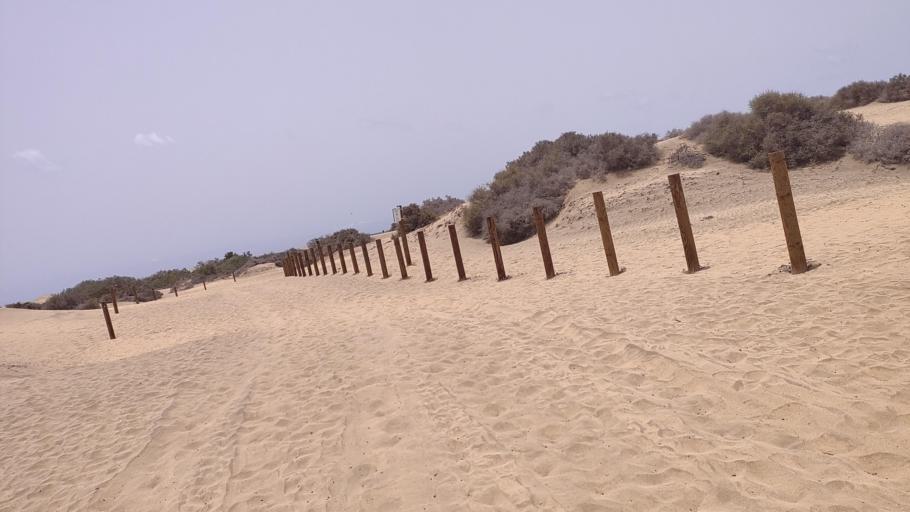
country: ES
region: Canary Islands
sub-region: Provincia de Las Palmas
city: Playa del Ingles
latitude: 27.7429
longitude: -15.5898
